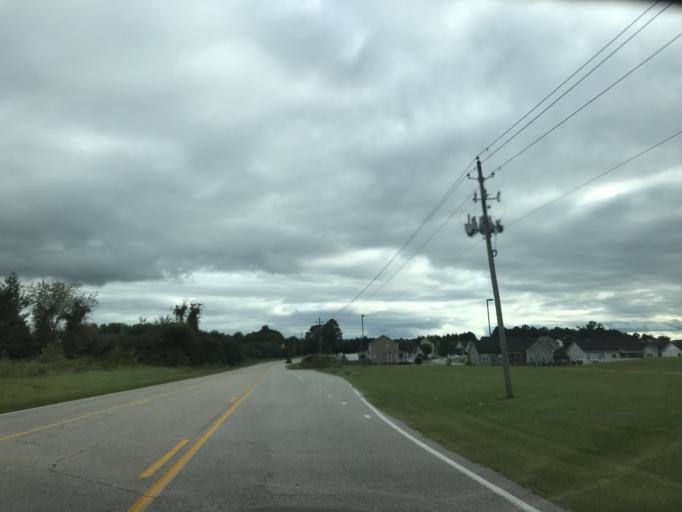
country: US
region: North Carolina
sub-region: Johnston County
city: Clayton
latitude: 35.5744
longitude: -78.5477
